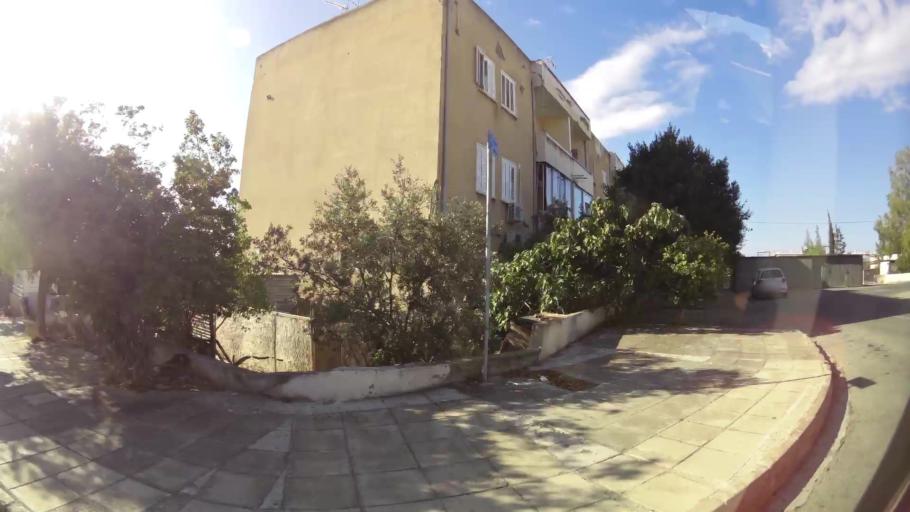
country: CY
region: Lefkosia
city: Nicosia
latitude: 35.1333
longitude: 33.3664
